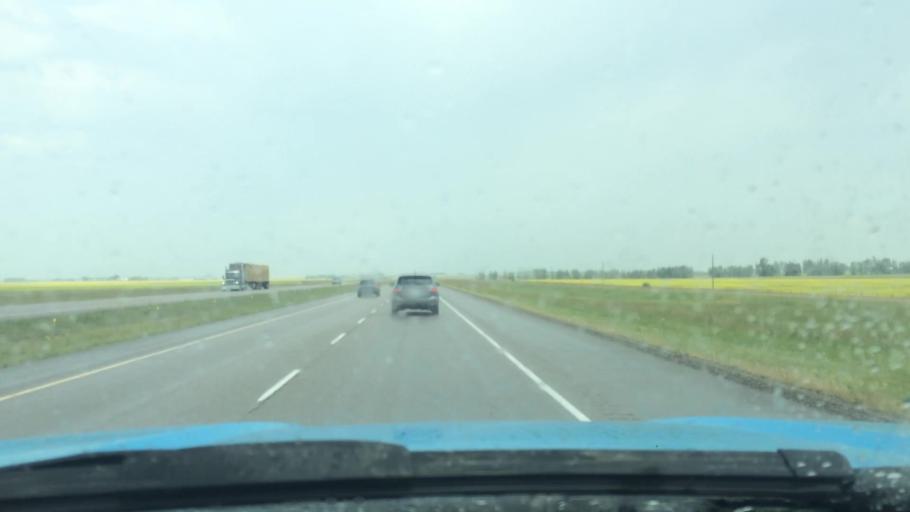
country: CA
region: Alberta
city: Carstairs
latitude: 51.6136
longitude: -114.0253
